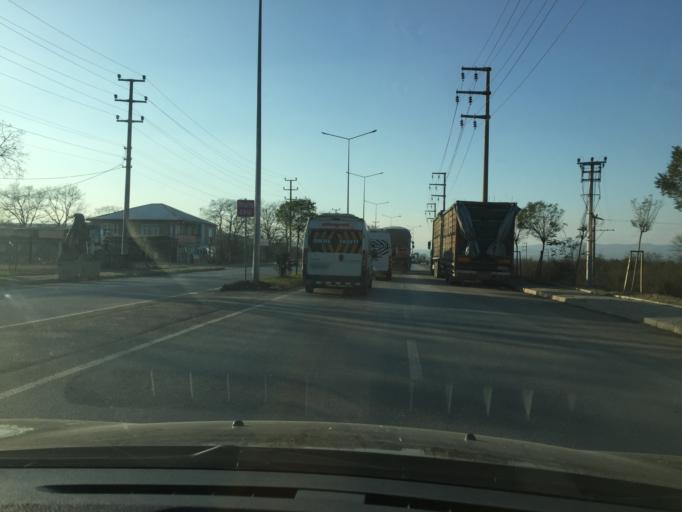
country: TR
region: Sakarya
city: Sogutlu
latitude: 40.8986
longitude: 30.5096
